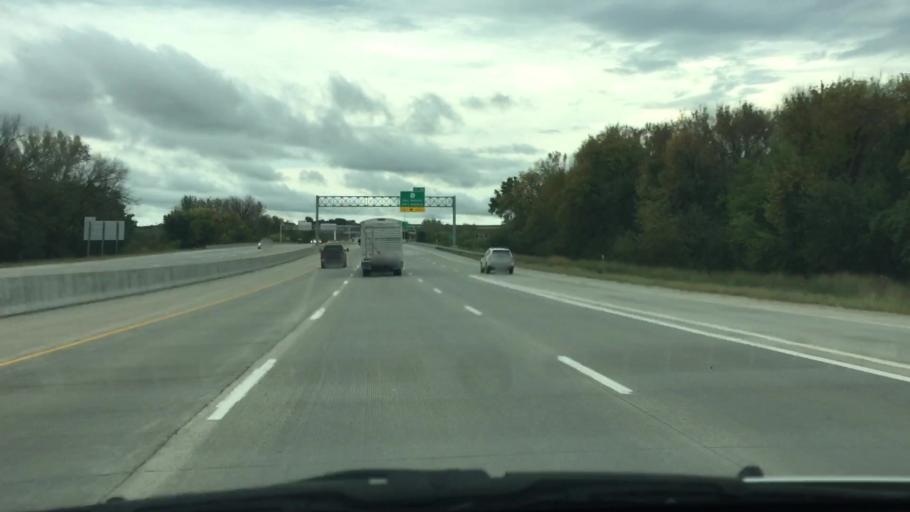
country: US
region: Iowa
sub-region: Polk County
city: West Des Moines
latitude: 41.5356
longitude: -93.7746
